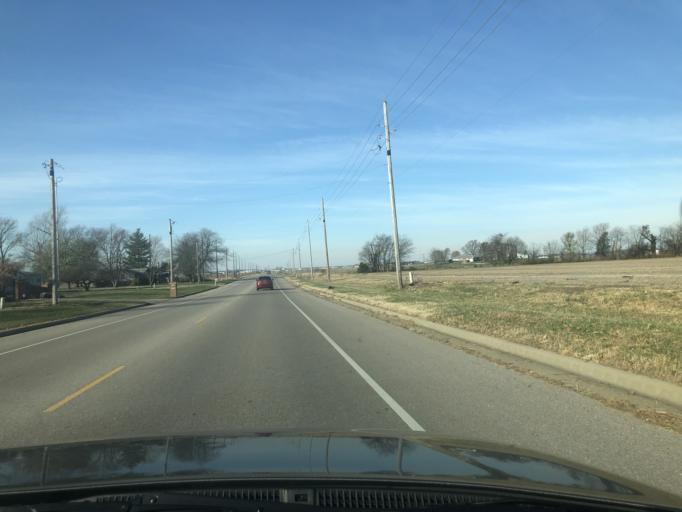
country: US
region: Indiana
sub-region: Warrick County
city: Newburgh
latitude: 37.9912
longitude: -87.4162
